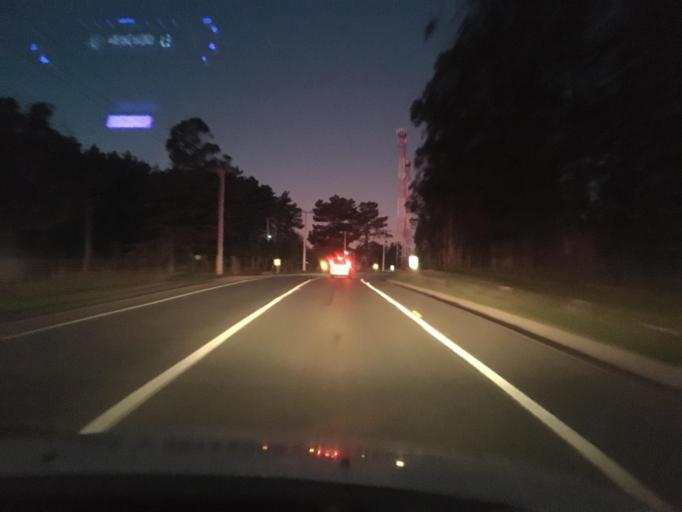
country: CL
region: Valparaiso
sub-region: San Antonio Province
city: El Tabo
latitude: -33.4248
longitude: -71.6622
